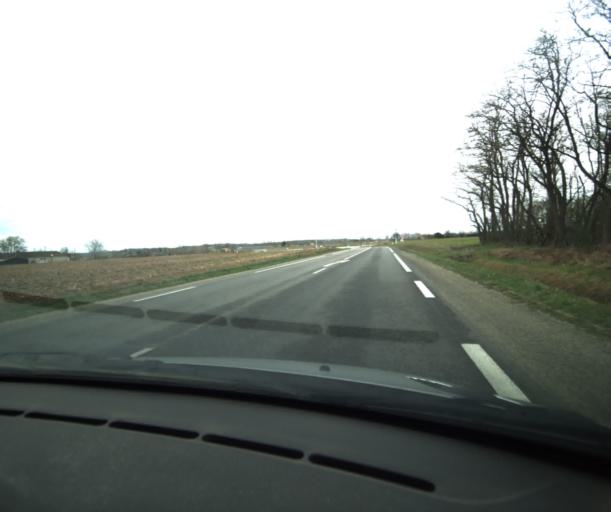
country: FR
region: Midi-Pyrenees
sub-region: Departement du Tarn-et-Garonne
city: Moissac
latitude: 44.0825
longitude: 1.1161
